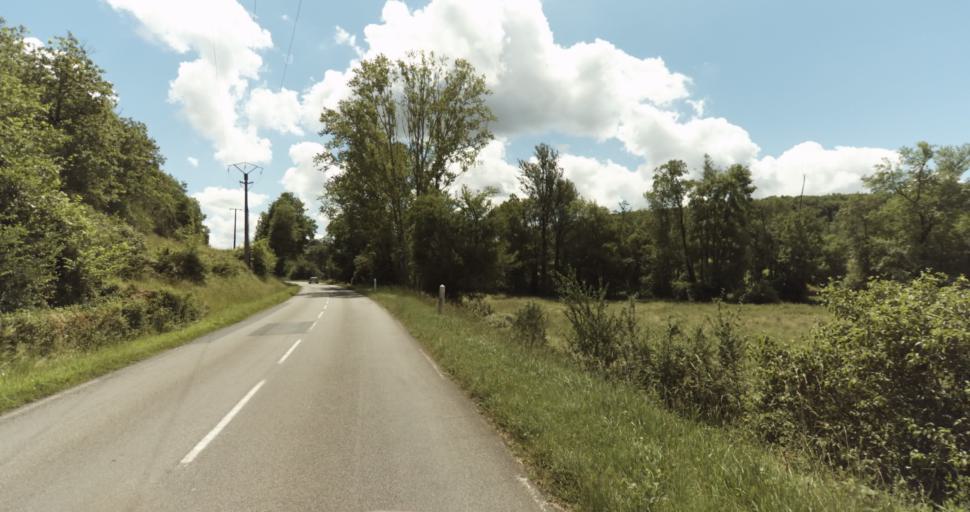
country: FR
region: Aquitaine
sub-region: Departement de la Dordogne
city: Lalinde
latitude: 44.7984
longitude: 0.7401
